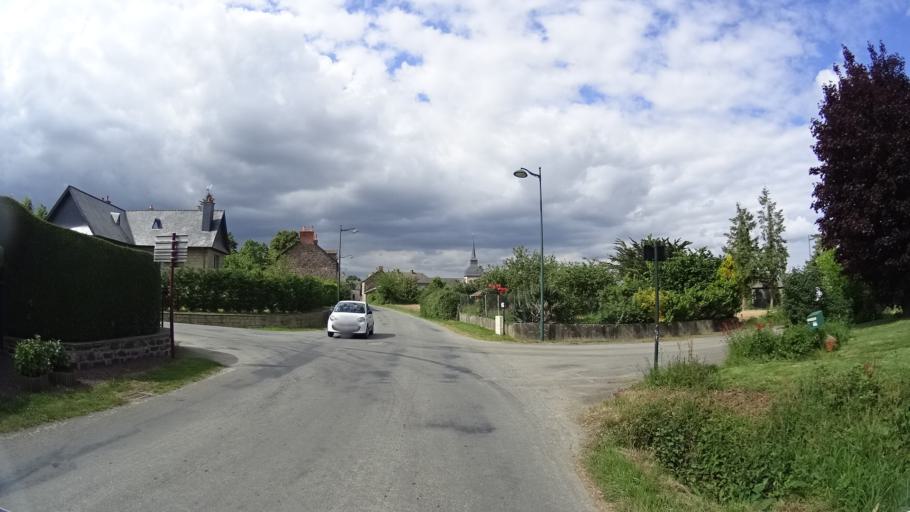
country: FR
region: Brittany
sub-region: Departement d'Ille-et-Vilaine
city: Iffendic
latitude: 48.0915
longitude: -2.0984
